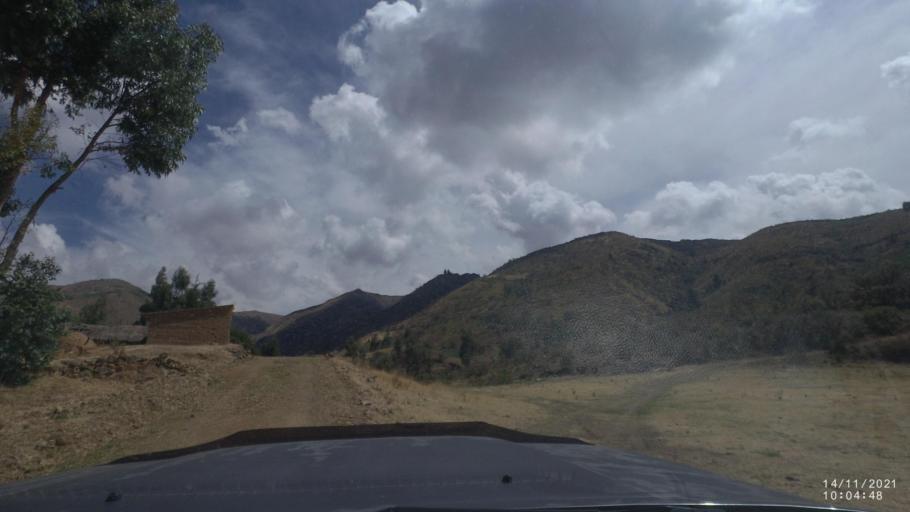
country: BO
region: Cochabamba
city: Cochabamba
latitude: -17.3490
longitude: -66.0919
